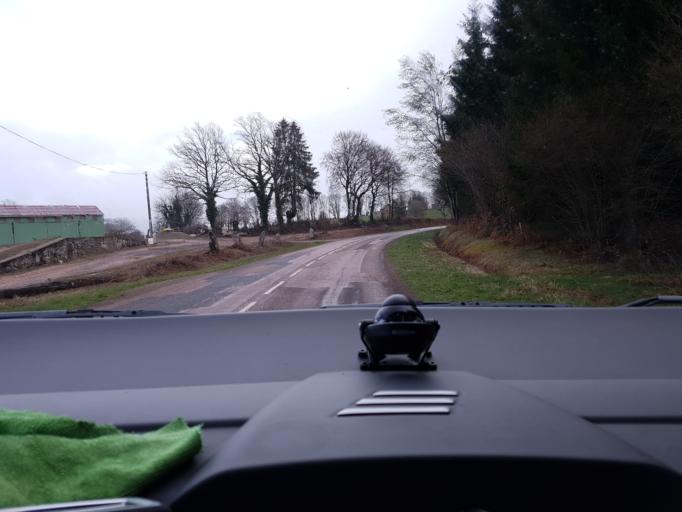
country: FR
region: Bourgogne
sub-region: Departement de la Cote-d'Or
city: Saulieu
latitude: 47.2741
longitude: 4.0269
